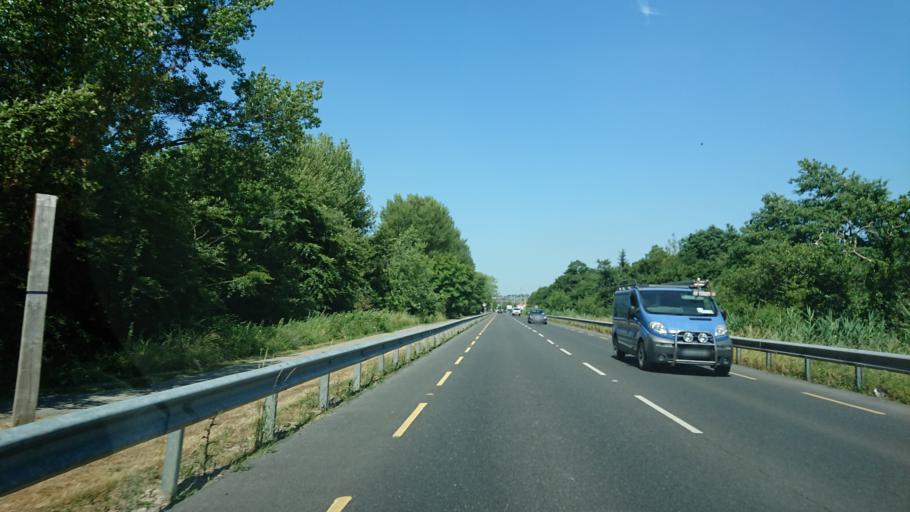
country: IE
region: Munster
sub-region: Waterford
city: Waterford
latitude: 52.2420
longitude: -7.1209
